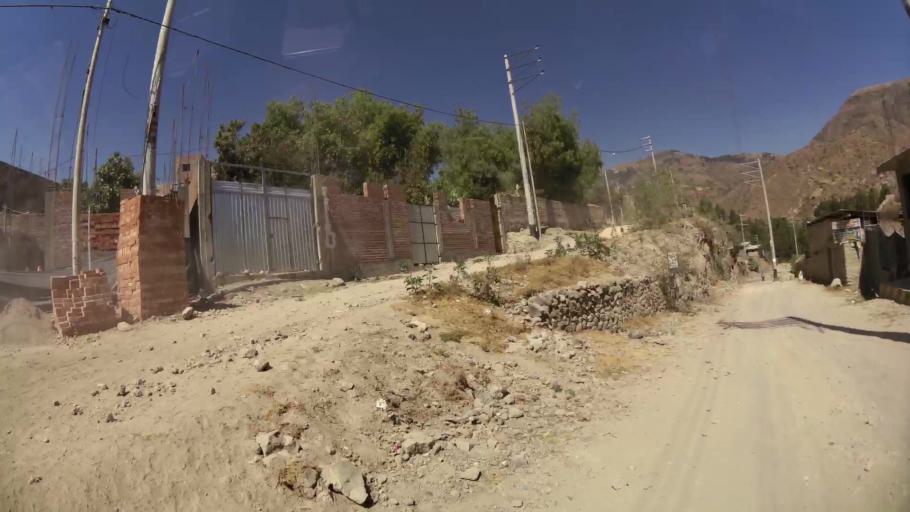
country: PE
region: Ayacucho
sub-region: Provincia de Huamanga
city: Carmen Alto
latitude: -13.1773
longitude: -74.2274
